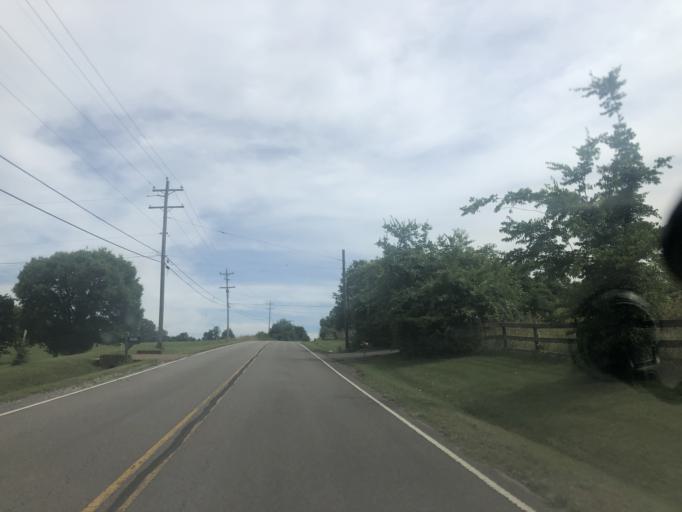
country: US
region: Tennessee
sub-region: Davidson County
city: Lakewood
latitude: 36.2163
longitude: -86.6668
